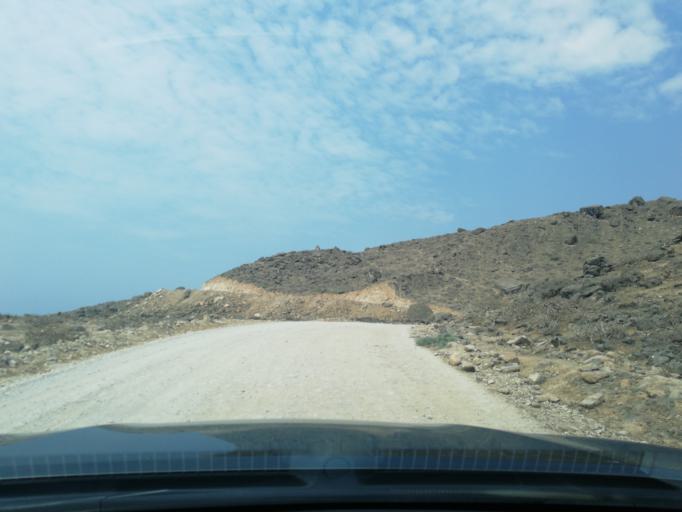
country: OM
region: Zufar
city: Salalah
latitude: 16.8212
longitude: 53.6970
